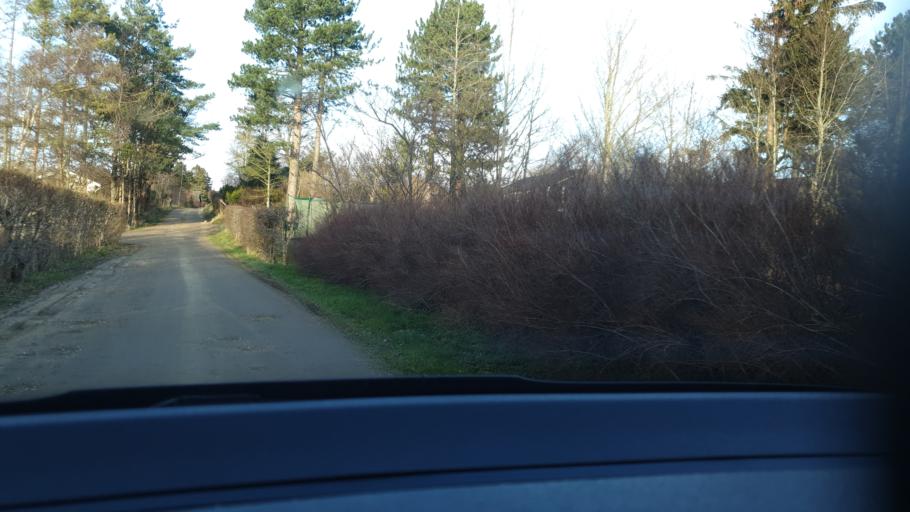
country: DK
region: Zealand
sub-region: Odsherred Kommune
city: Hojby
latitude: 55.9326
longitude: 11.6232
